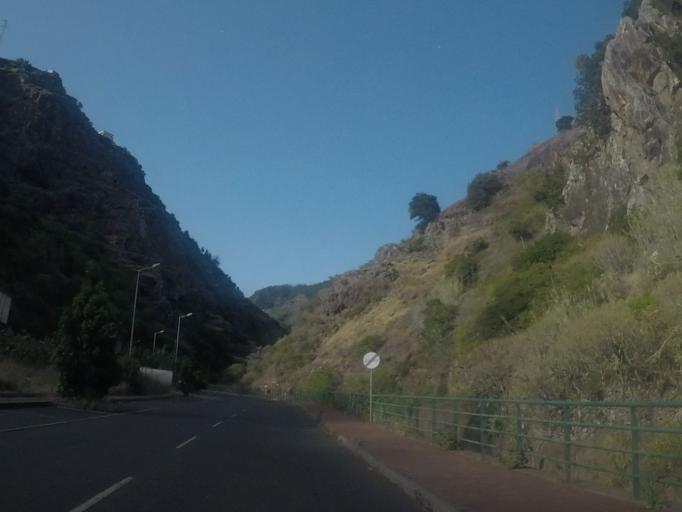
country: PT
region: Madeira
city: Ponta do Sol
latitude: 32.6871
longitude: -17.0973
